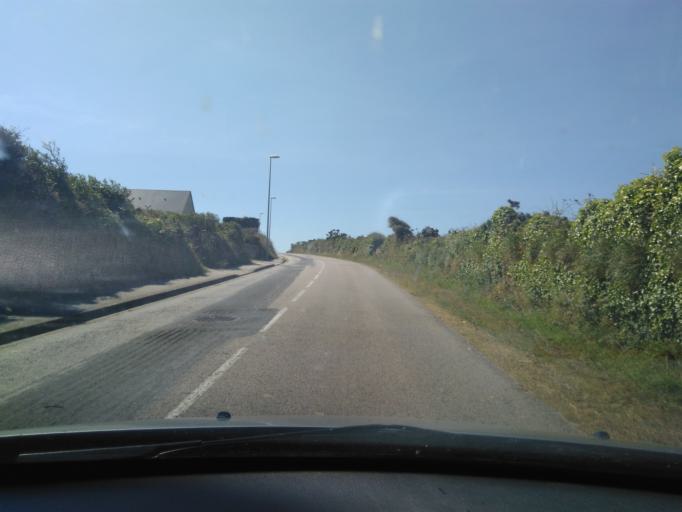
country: FR
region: Lower Normandy
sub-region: Departement de la Manche
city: Beaumont-Hague
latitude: 49.7086
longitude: -1.9320
